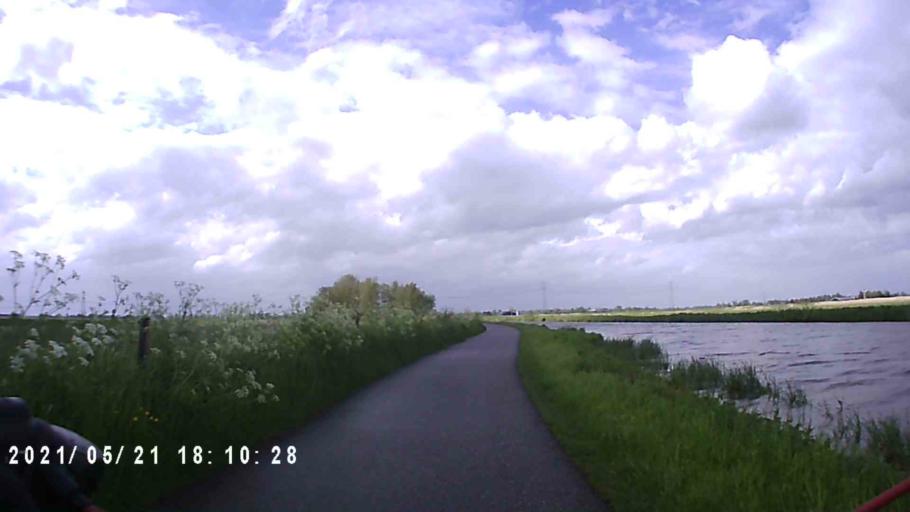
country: NL
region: Groningen
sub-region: Gemeente Zuidhorn
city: Zuidhorn
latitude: 53.2024
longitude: 6.4131
